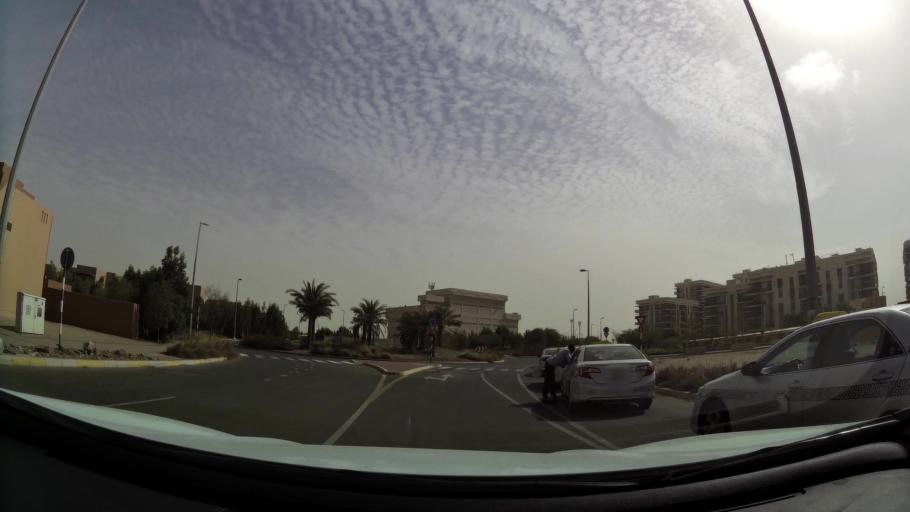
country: AE
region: Abu Dhabi
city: Abu Dhabi
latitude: 24.4126
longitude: 54.5376
